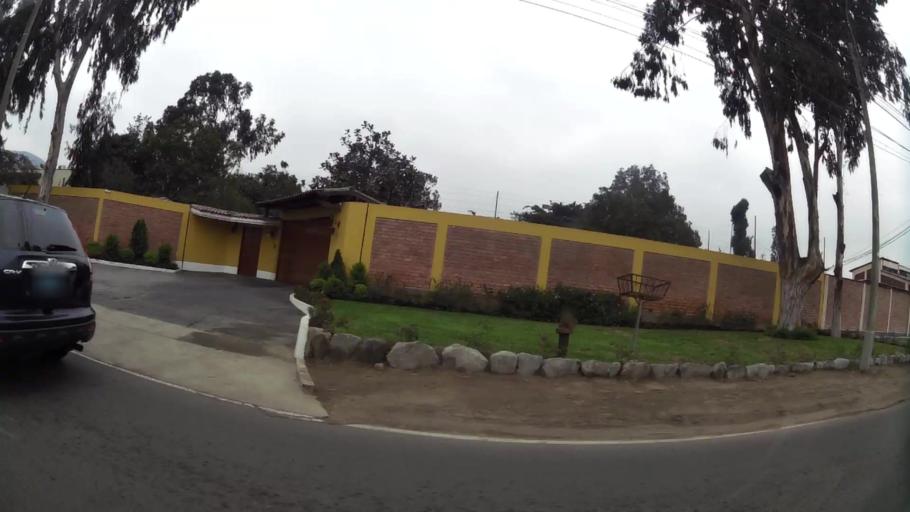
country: PE
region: Lima
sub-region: Lima
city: La Molina
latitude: -12.0816
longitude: -76.9148
